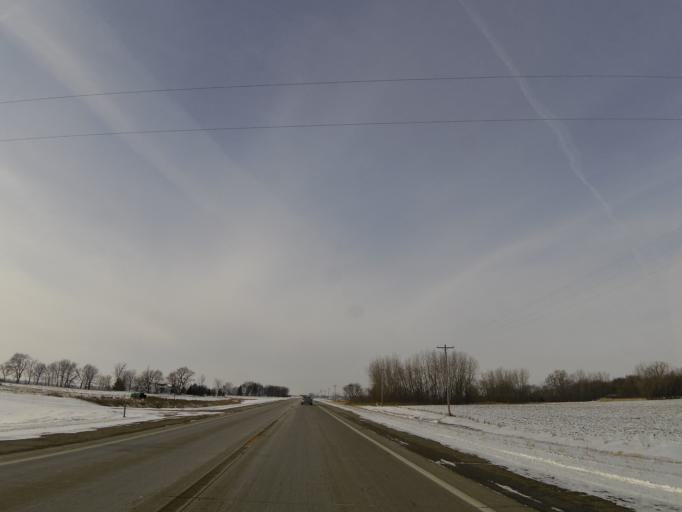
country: US
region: Minnesota
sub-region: McLeod County
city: Hutchinson
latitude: 44.8926
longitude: -94.2971
